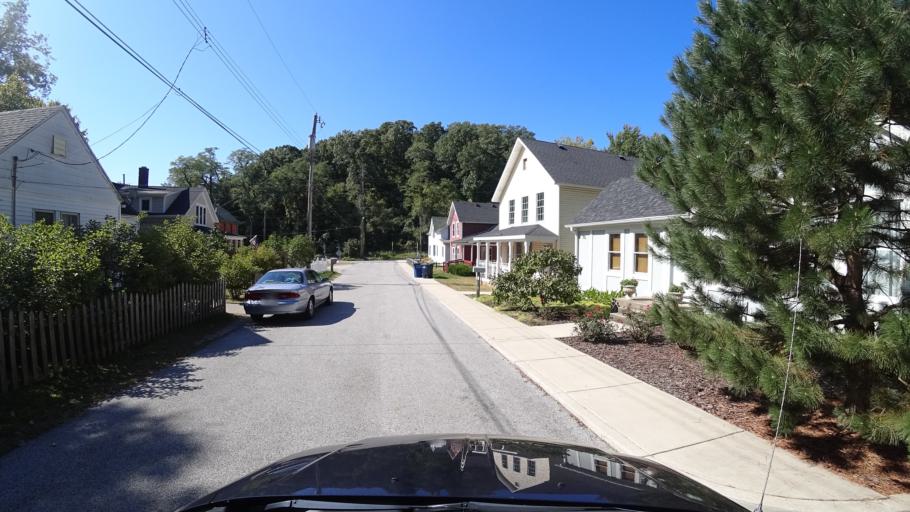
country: US
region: Indiana
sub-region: LaPorte County
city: Michigan City
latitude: 41.7238
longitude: -86.8939
